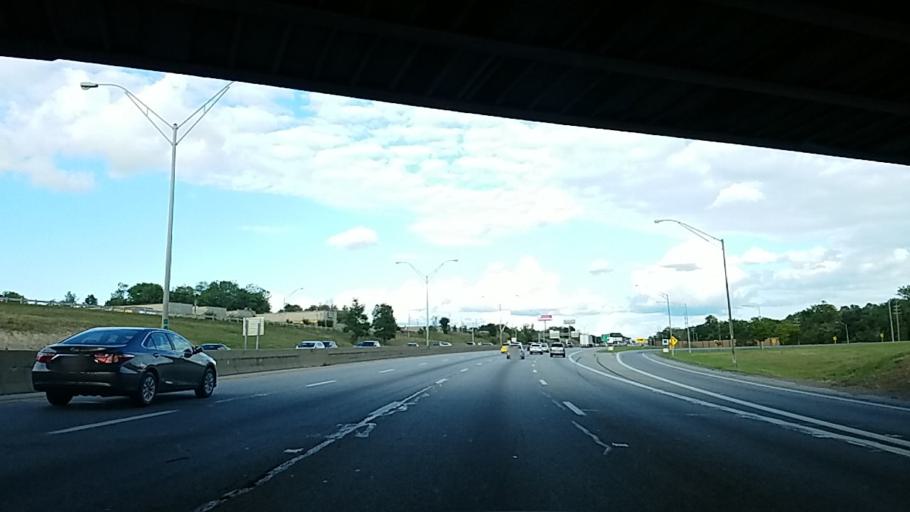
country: US
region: Ohio
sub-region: Cuyahoga County
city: Maple Heights
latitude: 41.4243
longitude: -81.5791
